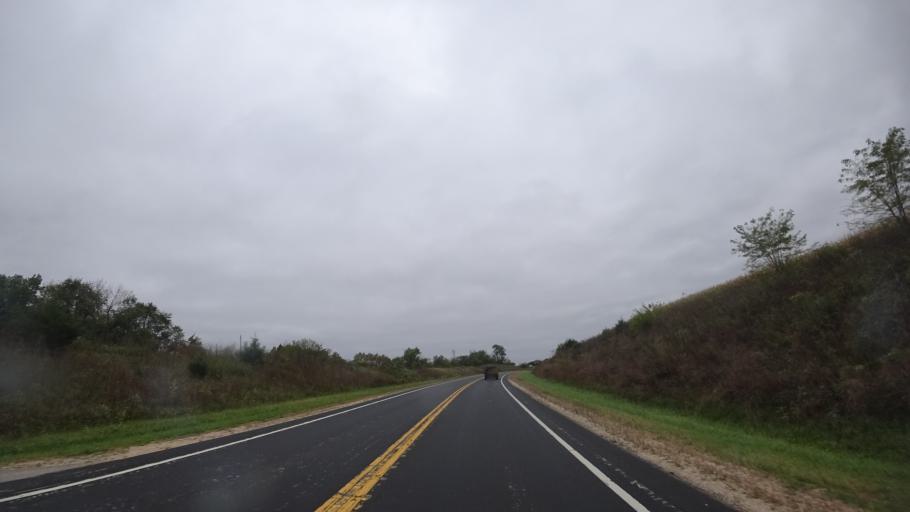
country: US
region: Wisconsin
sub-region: Grant County
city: Boscobel
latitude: 43.1132
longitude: -90.7950
